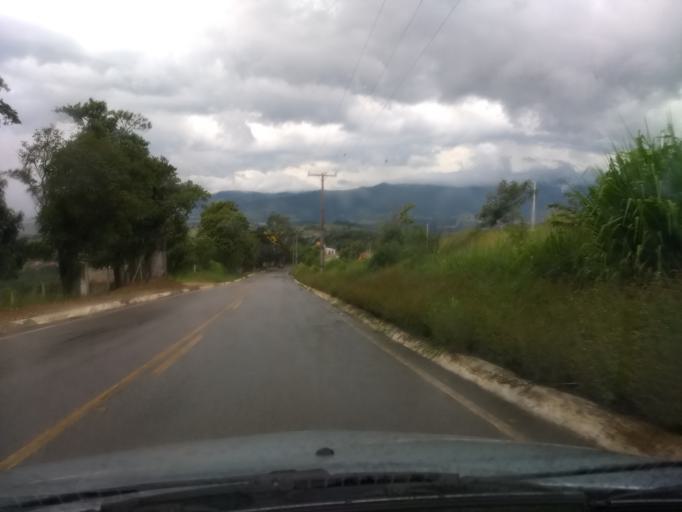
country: BR
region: Minas Gerais
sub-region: Extrema
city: Extrema
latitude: -22.7991
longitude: -46.3154
